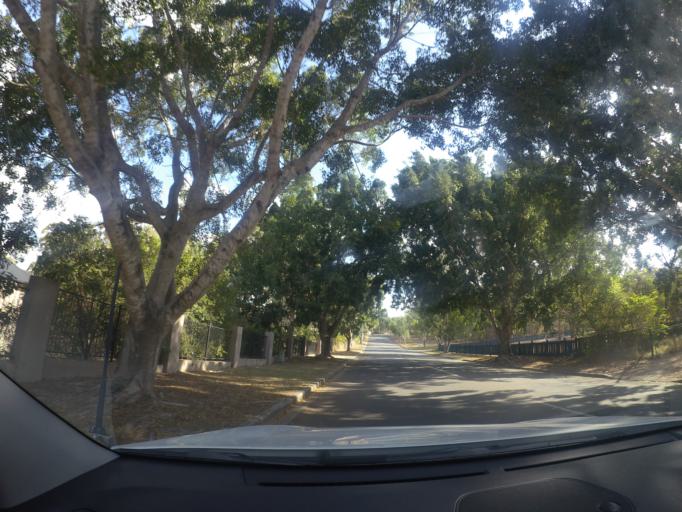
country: AU
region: Queensland
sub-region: Logan
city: Woodridge
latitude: -27.6519
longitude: 153.0638
